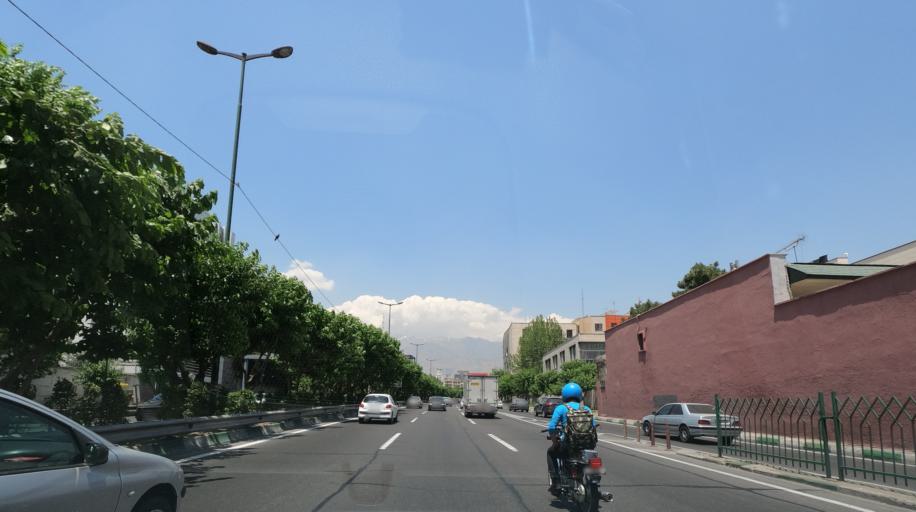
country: IR
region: Tehran
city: Tajrish
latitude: 35.7635
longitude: 51.4214
